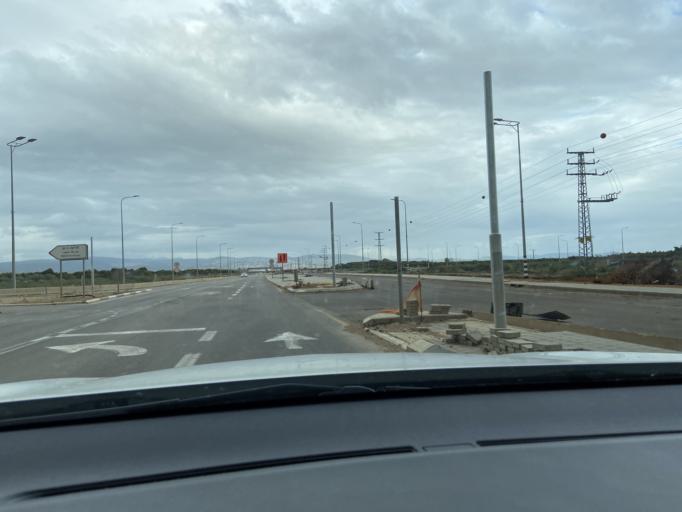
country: IL
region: Northern District
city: El Mazra`a
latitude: 32.9796
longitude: 35.1062
